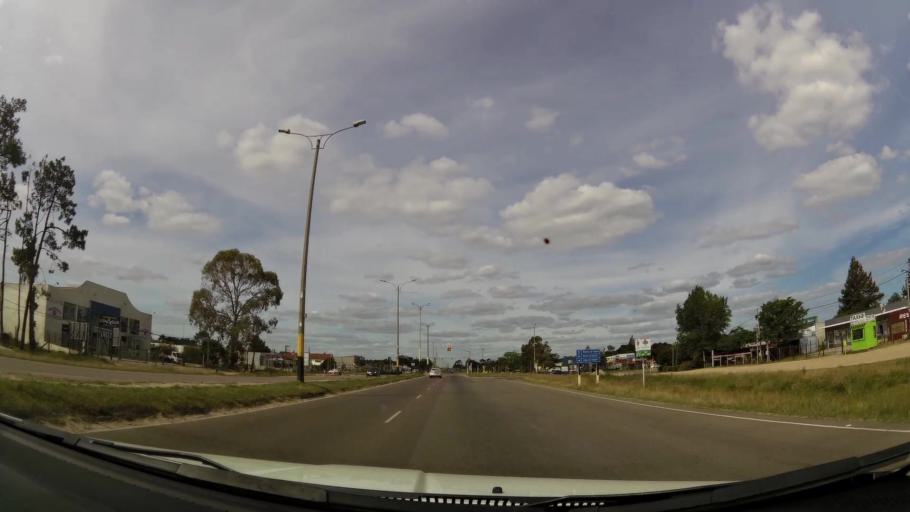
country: UY
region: Canelones
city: Colonia Nicolich
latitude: -34.8167
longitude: -55.9487
